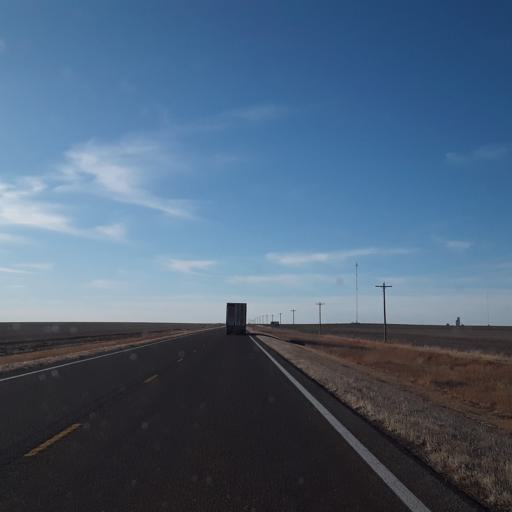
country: US
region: Kansas
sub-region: Cheyenne County
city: Saint Francis
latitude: 39.7566
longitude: -101.6770
